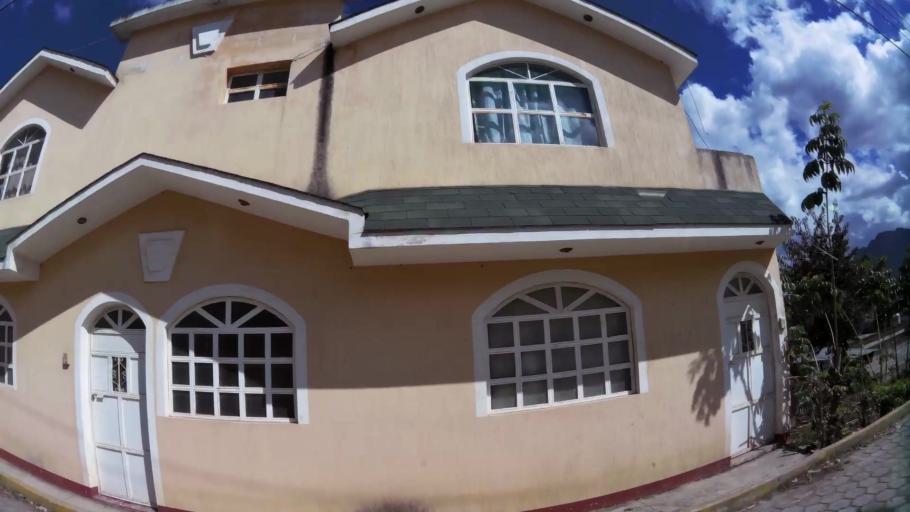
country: GT
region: Quetzaltenango
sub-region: Municipio de La Esperanza
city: La Esperanza
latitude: 14.8431
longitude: -91.5485
